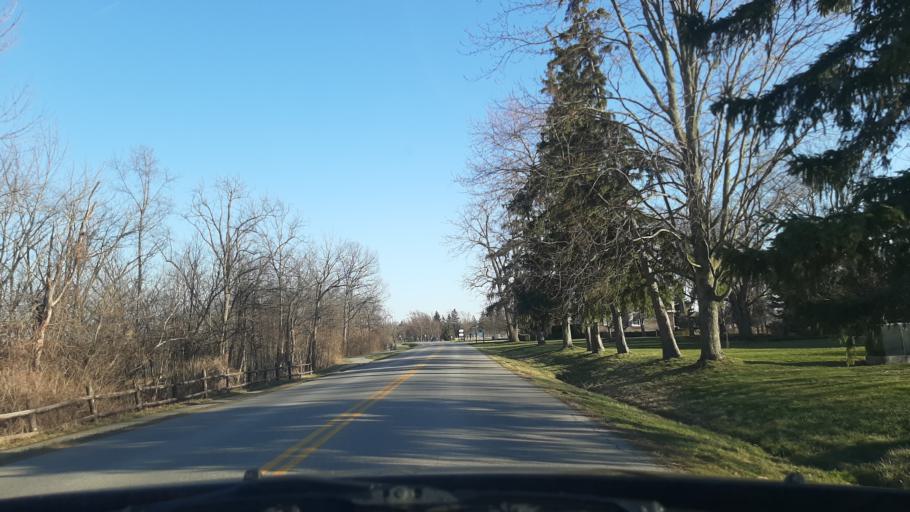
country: US
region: New York
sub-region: Niagara County
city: Youngstown
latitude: 43.2073
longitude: -79.0601
